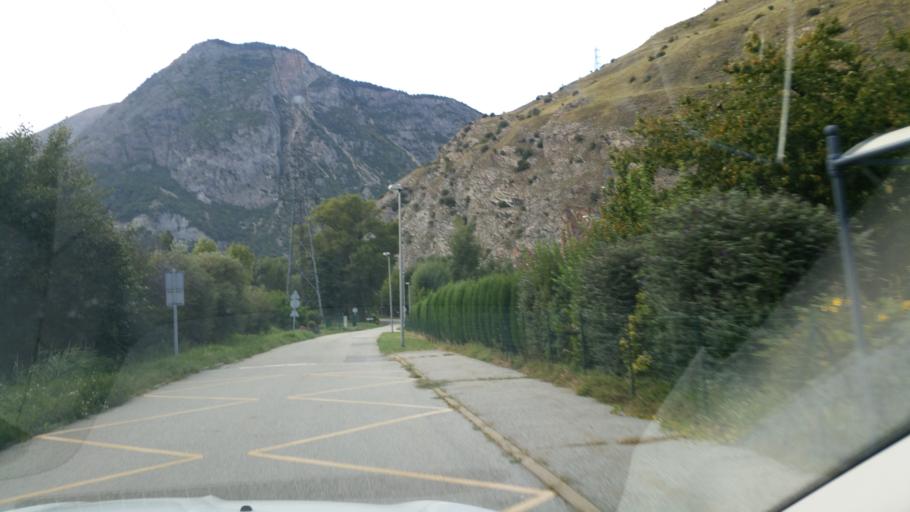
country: FR
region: Rhone-Alpes
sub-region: Departement de la Savoie
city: Villargondran
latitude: 45.2768
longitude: 6.3652
